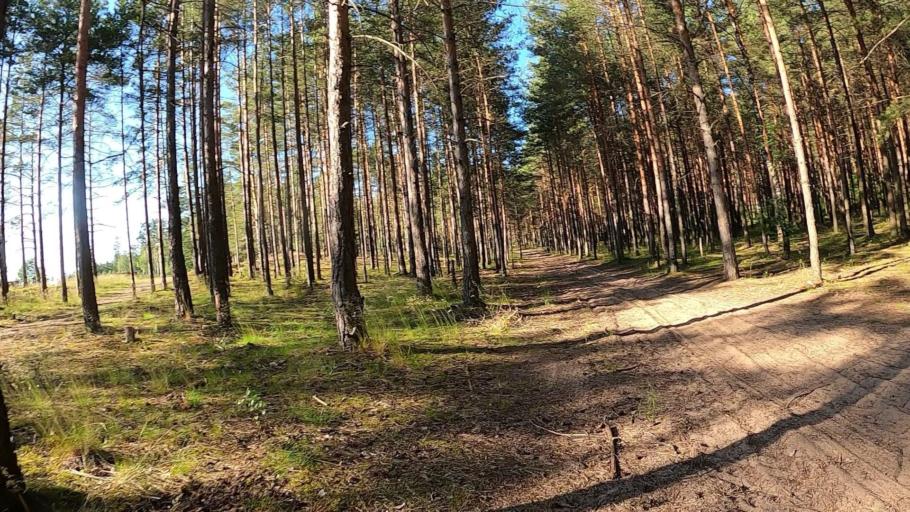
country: LV
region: Stopini
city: Ulbroka
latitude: 56.8813
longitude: 24.3000
